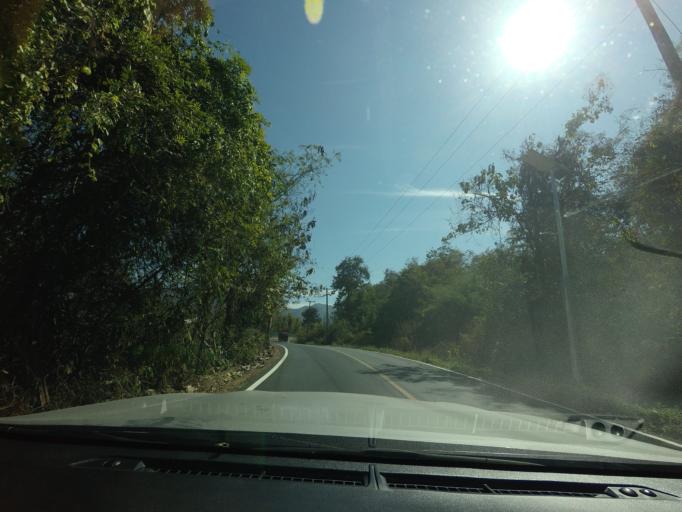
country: TH
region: Mae Hong Son
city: Wiang Nuea
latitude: 19.3779
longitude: 98.4345
